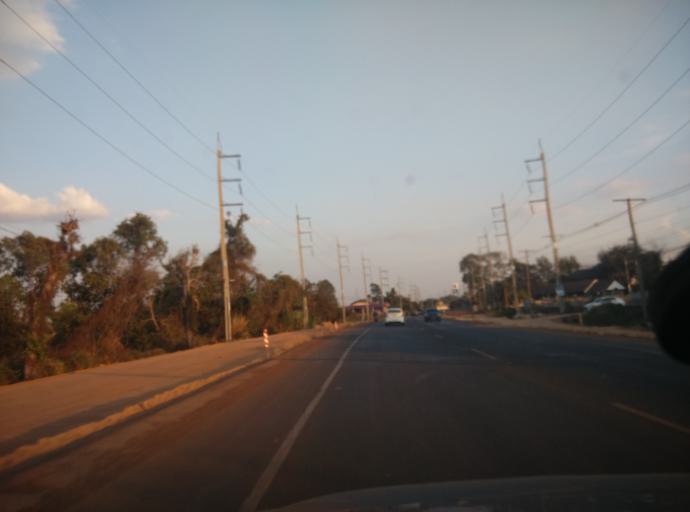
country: TH
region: Sisaket
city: Si Sa Ket
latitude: 15.1365
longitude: 104.2672
